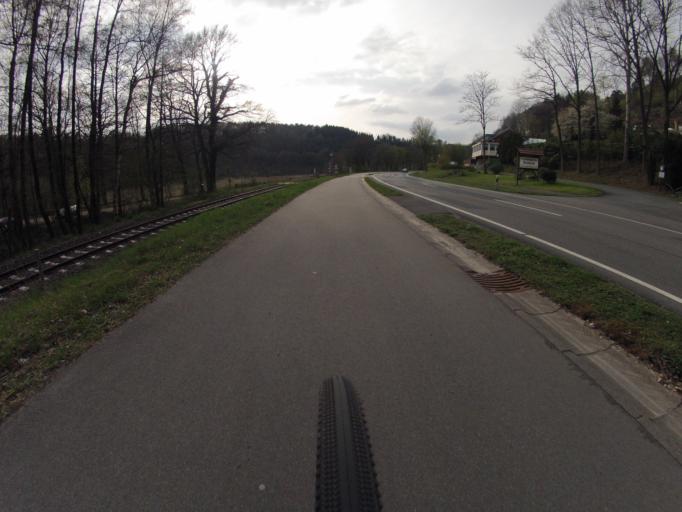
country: DE
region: North Rhine-Westphalia
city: Ibbenburen
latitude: 52.2343
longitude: 7.7460
